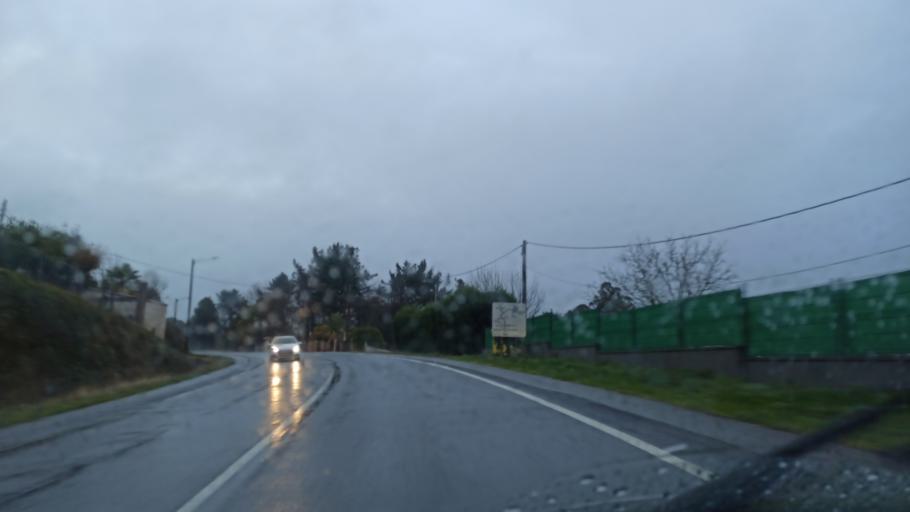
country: ES
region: Galicia
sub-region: Provincia da Coruna
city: Cesuras
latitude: 43.1964
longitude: -8.1729
